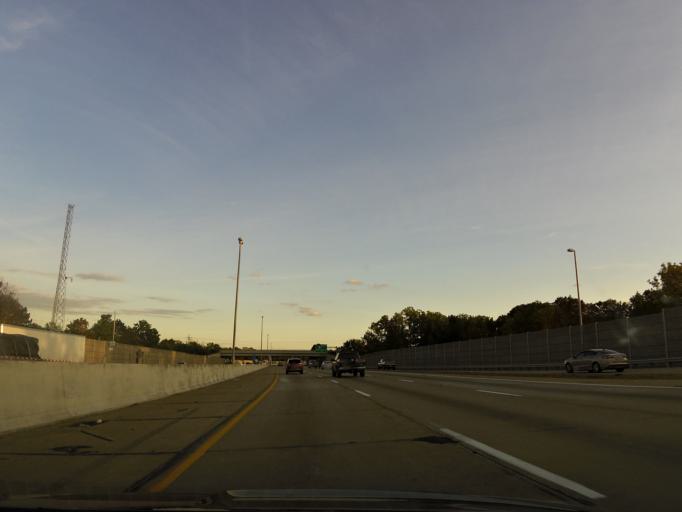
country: US
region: Indiana
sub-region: Marion County
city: Warren Park
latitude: 39.7918
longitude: -86.0353
